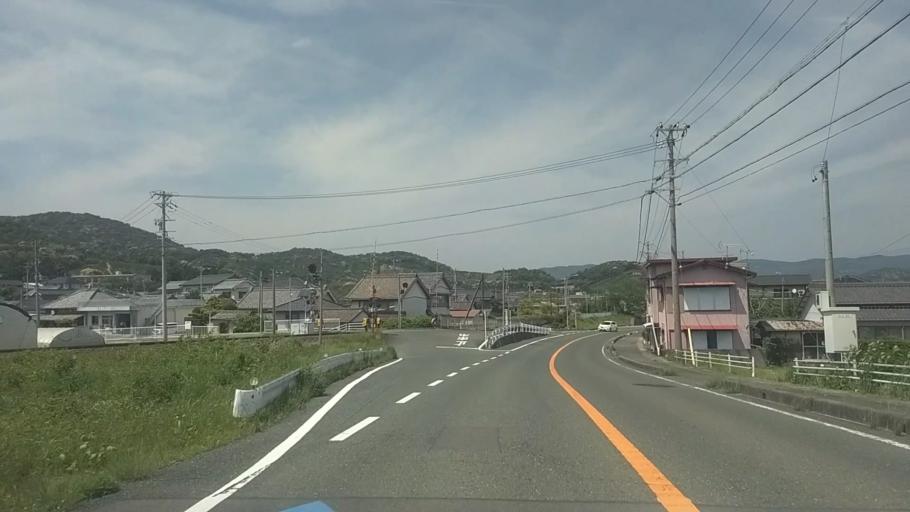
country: JP
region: Shizuoka
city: Kosai-shi
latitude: 34.7819
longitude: 137.5415
